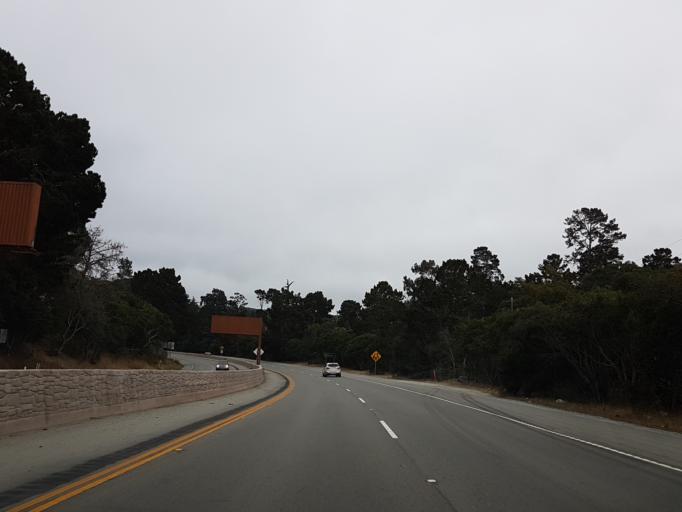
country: US
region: California
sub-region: Monterey County
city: Seaside
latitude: 36.5914
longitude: -121.8672
